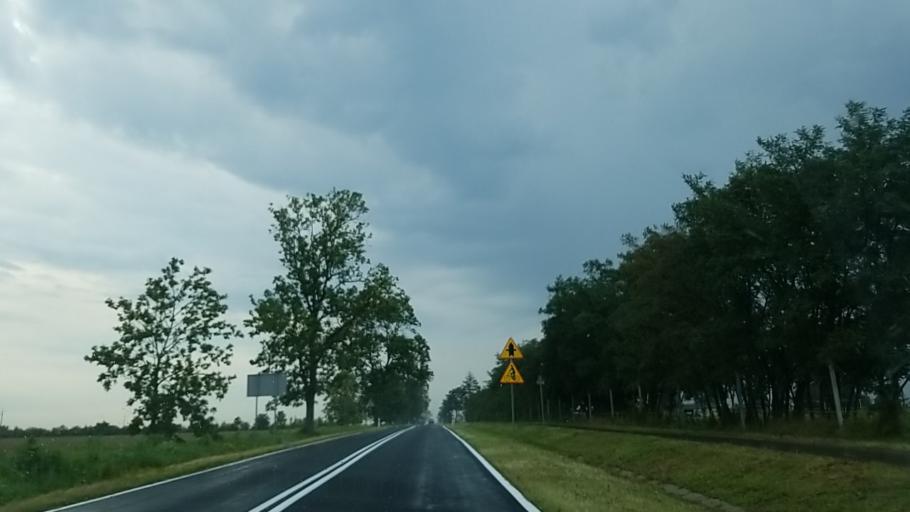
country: PL
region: Lublin Voivodeship
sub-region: Powiat wlodawski
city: Wlodawa
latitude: 51.6092
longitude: 23.5303
